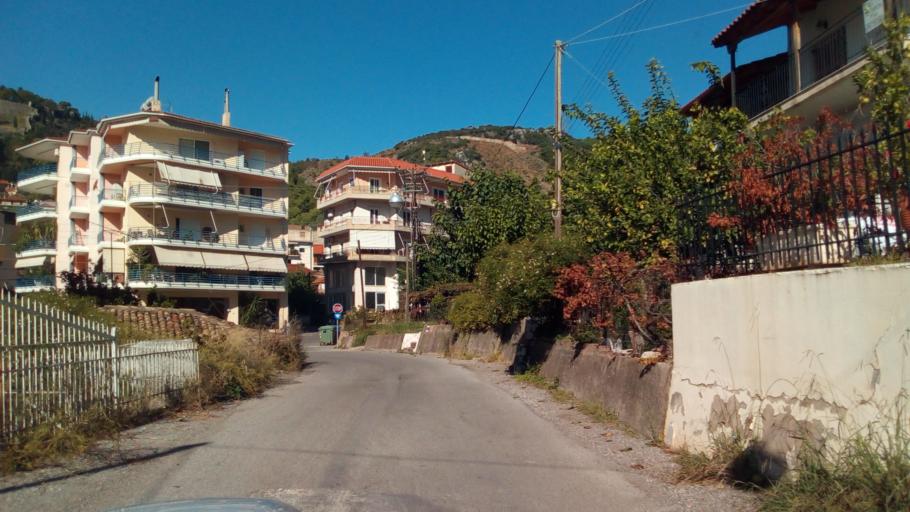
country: GR
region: West Greece
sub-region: Nomos Aitolias kai Akarnanias
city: Nafpaktos
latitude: 38.3967
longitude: 21.8332
